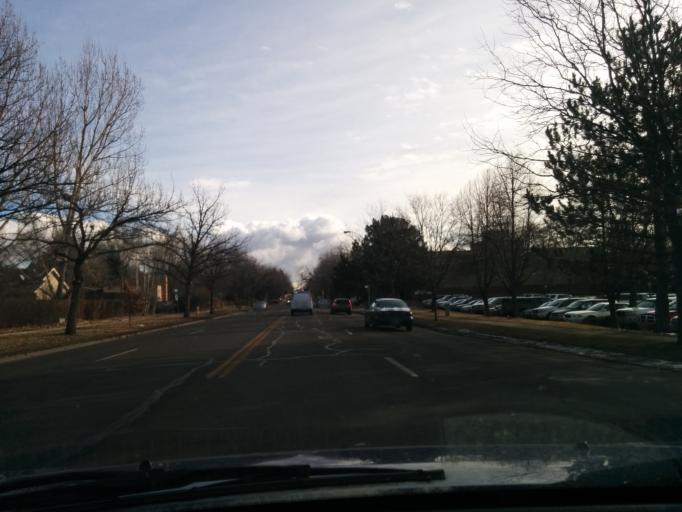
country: US
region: Colorado
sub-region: Larimer County
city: Fort Collins
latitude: 40.5671
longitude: -105.0559
